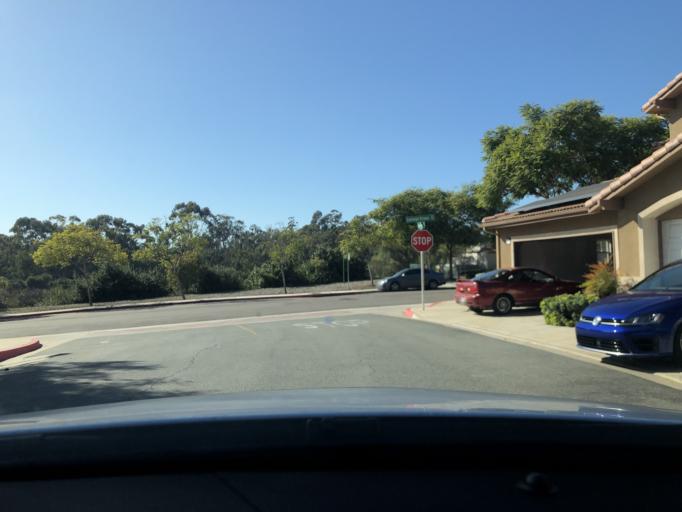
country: US
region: California
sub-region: San Diego County
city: Lemon Grove
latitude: 32.7389
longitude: -117.0588
